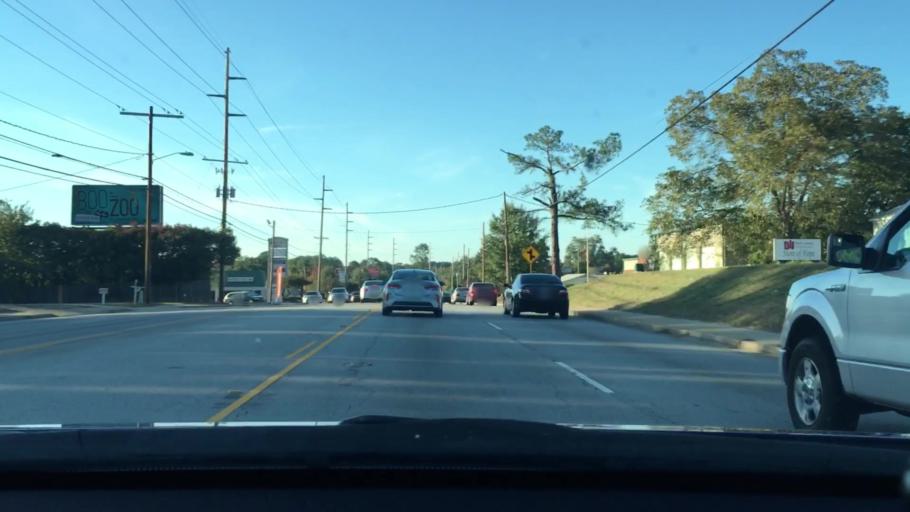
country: US
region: South Carolina
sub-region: Lexington County
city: Saint Andrews
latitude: 34.0516
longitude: -81.1072
